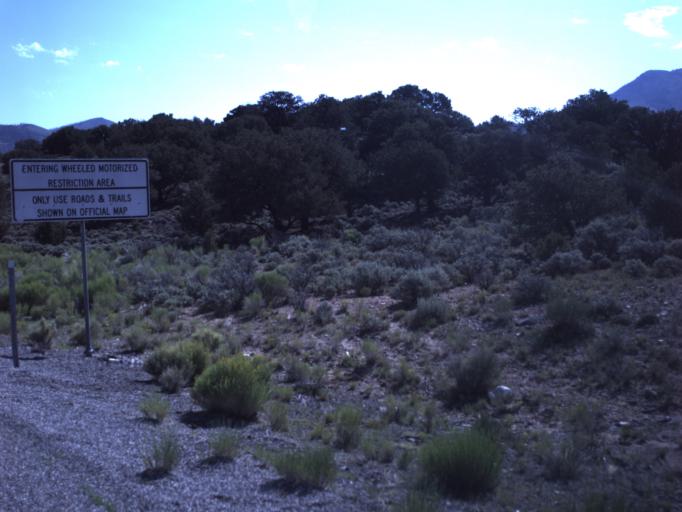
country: US
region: Utah
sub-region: Wayne County
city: Loa
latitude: 38.4901
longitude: -111.5411
